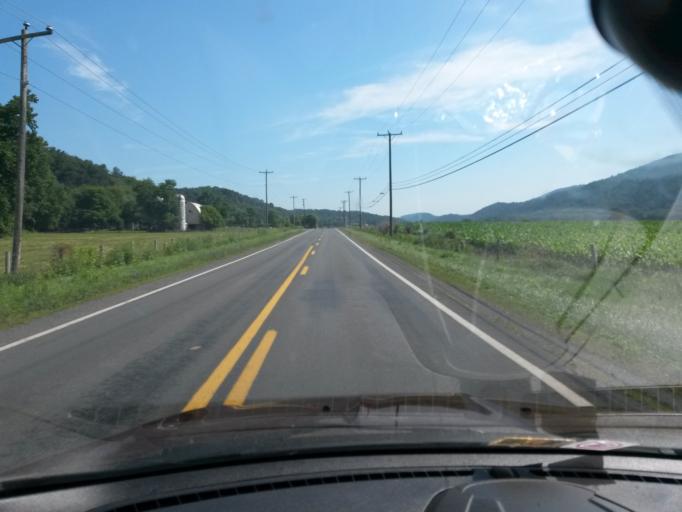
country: US
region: Virginia
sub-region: Shenandoah County
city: Basye
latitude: 38.9679
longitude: -78.8017
